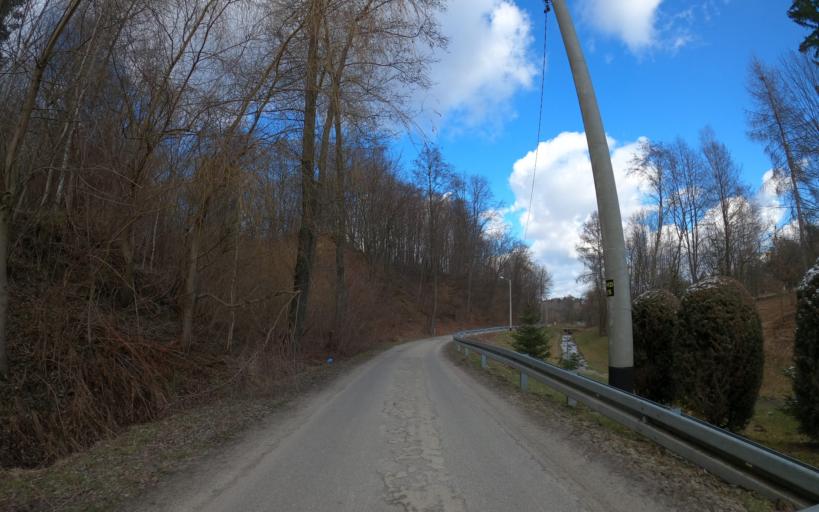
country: PL
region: Subcarpathian Voivodeship
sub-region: Powiat debicki
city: Debica
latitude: 50.0291
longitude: 21.4350
